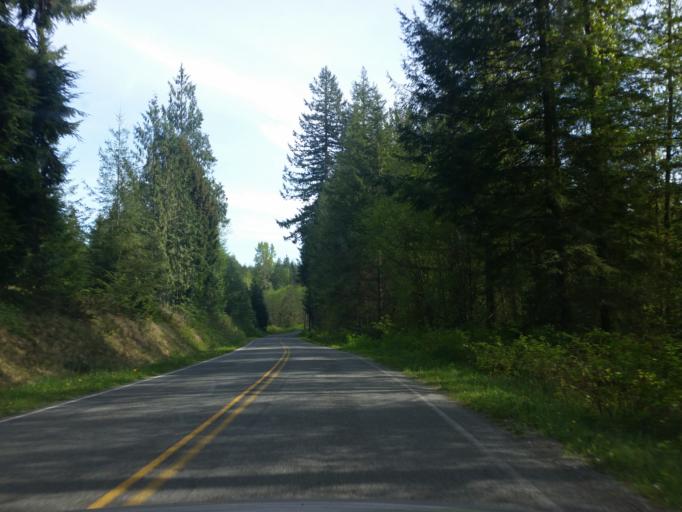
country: US
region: Washington
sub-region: Snohomish County
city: Granite Falls
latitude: 48.0505
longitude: -121.9245
